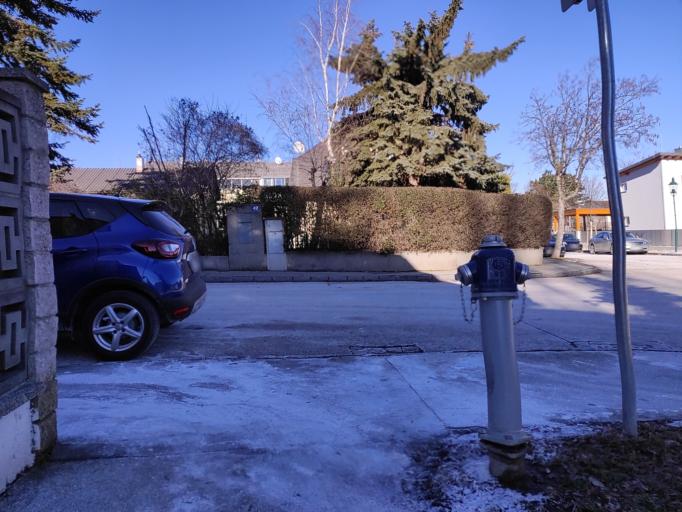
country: AT
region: Lower Austria
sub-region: Politischer Bezirk Modling
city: Brunn am Gebirge
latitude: 48.1098
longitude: 16.2815
